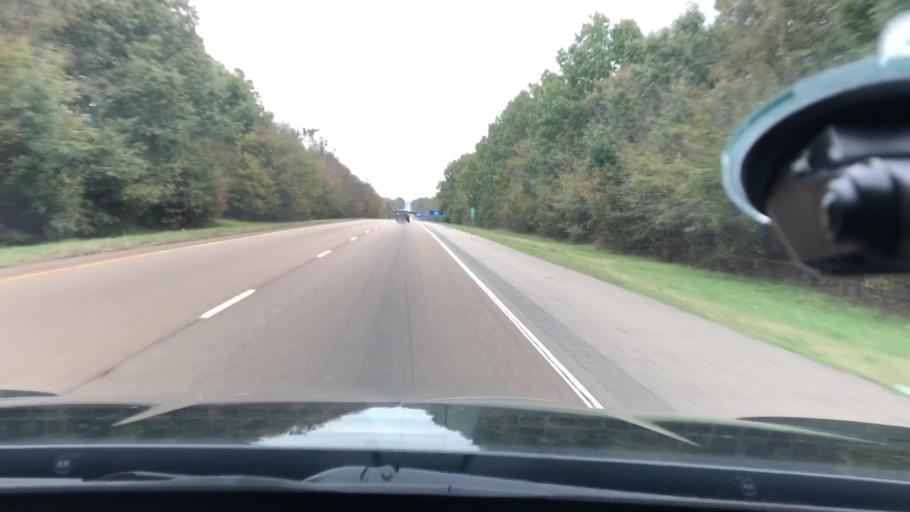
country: US
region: Arkansas
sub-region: Nevada County
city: Prescott
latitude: 33.7913
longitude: -93.4495
